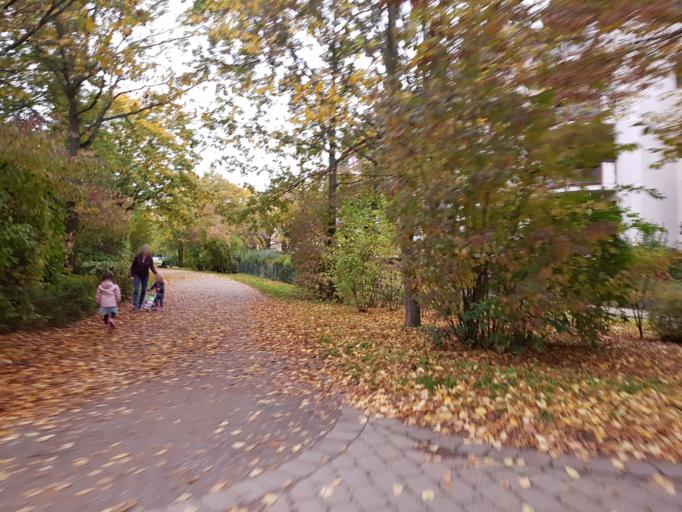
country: DE
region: Hesse
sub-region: Regierungsbezirk Darmstadt
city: Frankfurt am Main
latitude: 50.1453
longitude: 8.6710
